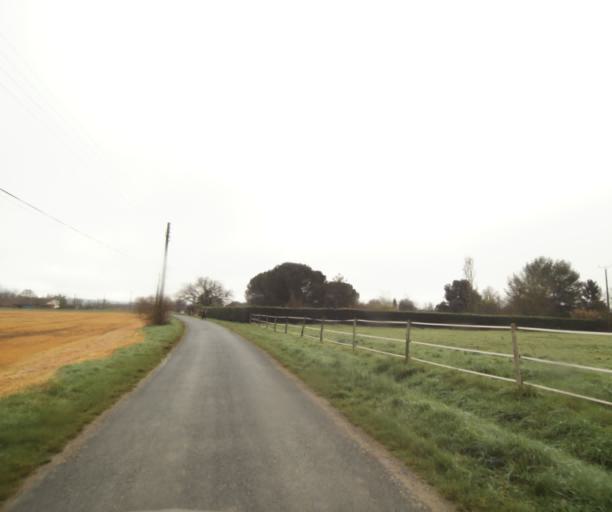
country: FR
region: Midi-Pyrenees
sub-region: Departement du Tarn-et-Garonne
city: Nohic
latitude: 43.8802
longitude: 1.4607
